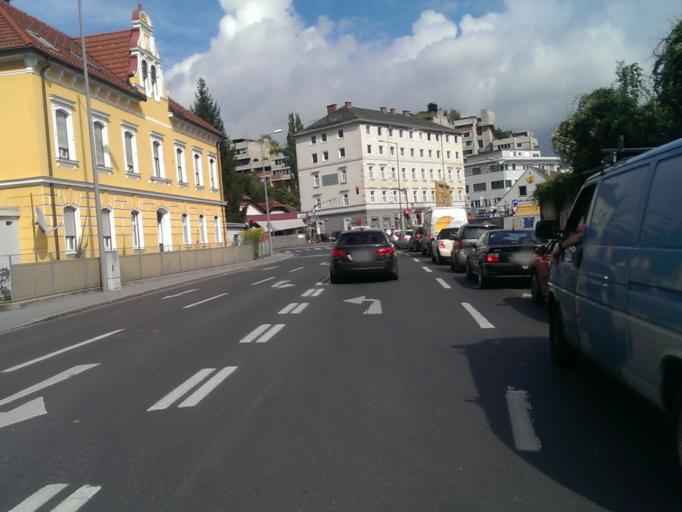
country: AT
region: Styria
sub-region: Graz Stadt
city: Graz
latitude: 47.0594
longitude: 15.4685
